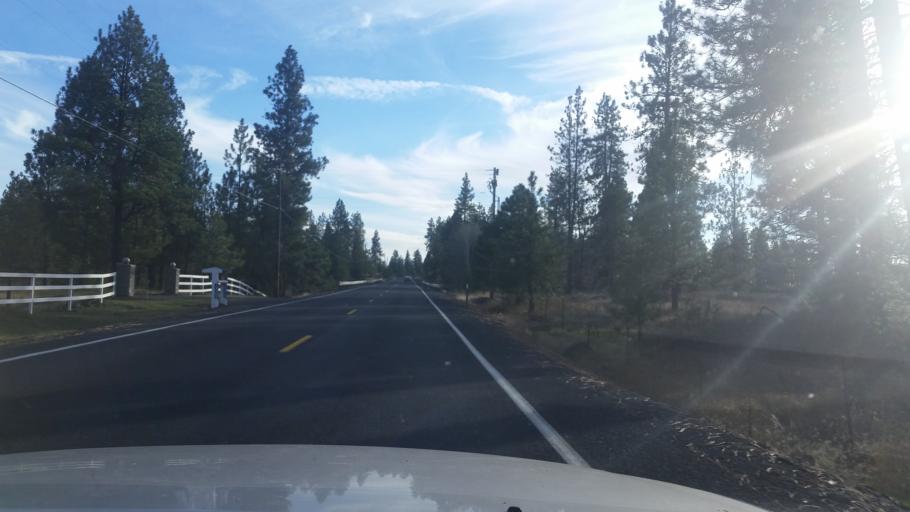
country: US
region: Washington
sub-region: Spokane County
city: Cheney
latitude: 47.4710
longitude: -117.5812
